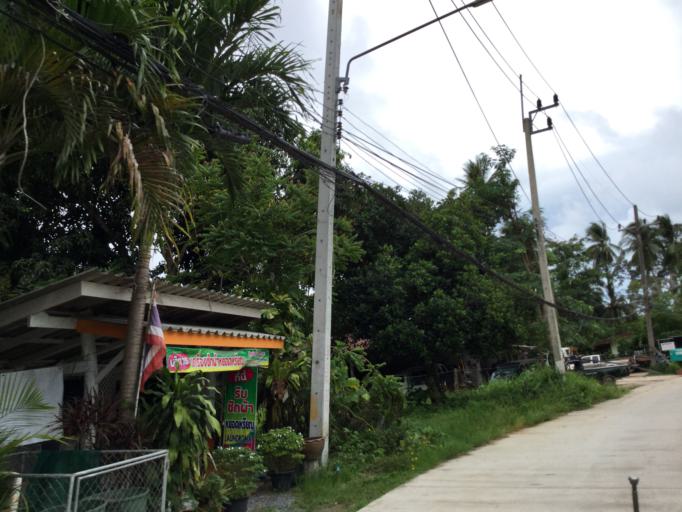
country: TH
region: Surat Thani
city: Ko Pha-Ngan
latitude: 9.7081
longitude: 100.0289
